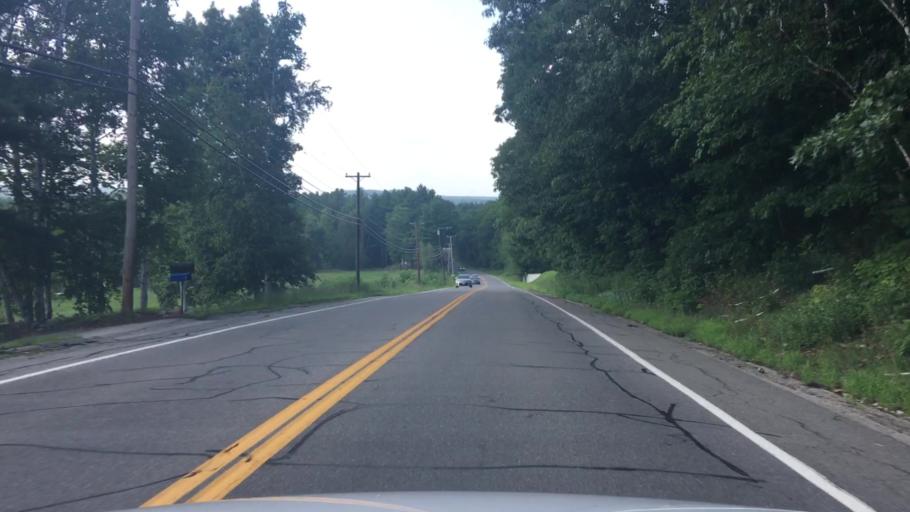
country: US
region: New Hampshire
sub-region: Rockingham County
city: Auburn
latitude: 42.9753
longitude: -71.3680
